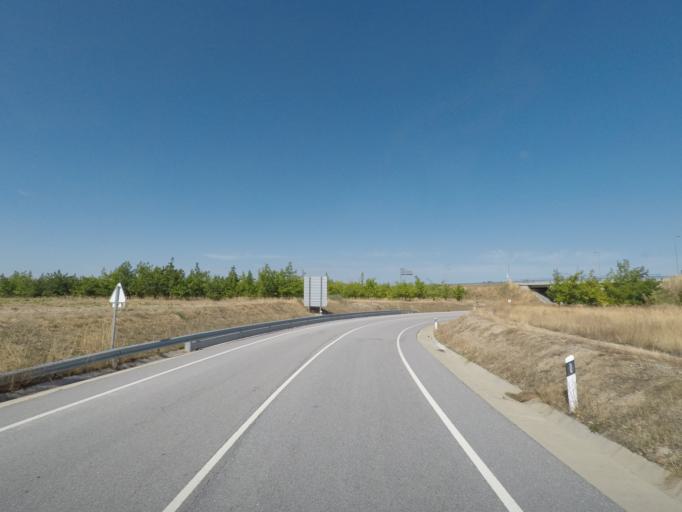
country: ES
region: Castille and Leon
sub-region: Provincia de Salamanca
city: Villarino de los Aires
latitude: 41.3678
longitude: -6.5058
